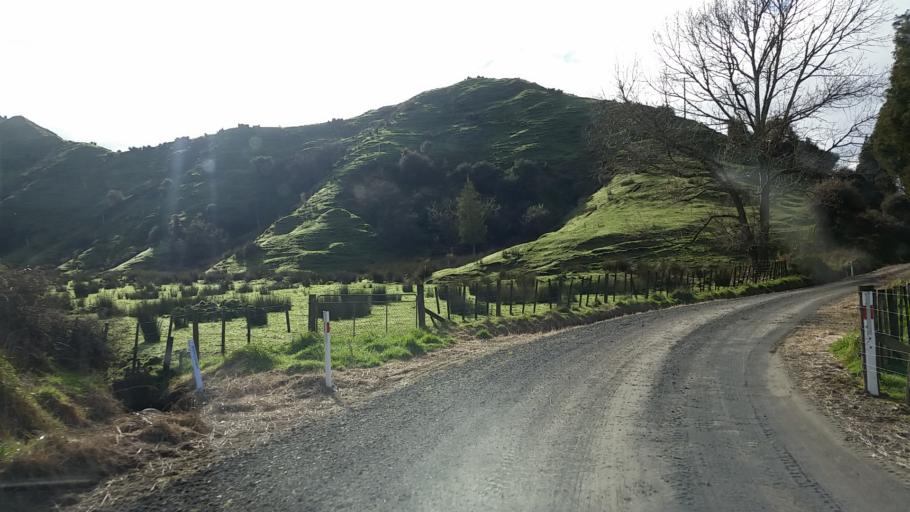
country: NZ
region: Taranaki
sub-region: South Taranaki District
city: Eltham
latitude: -39.2558
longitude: 174.5262
